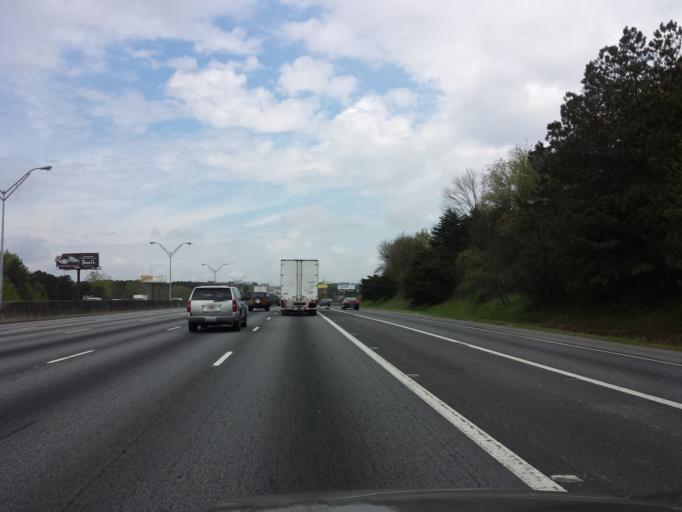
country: US
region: Georgia
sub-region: Cobb County
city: Marietta
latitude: 33.9652
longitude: -84.5229
